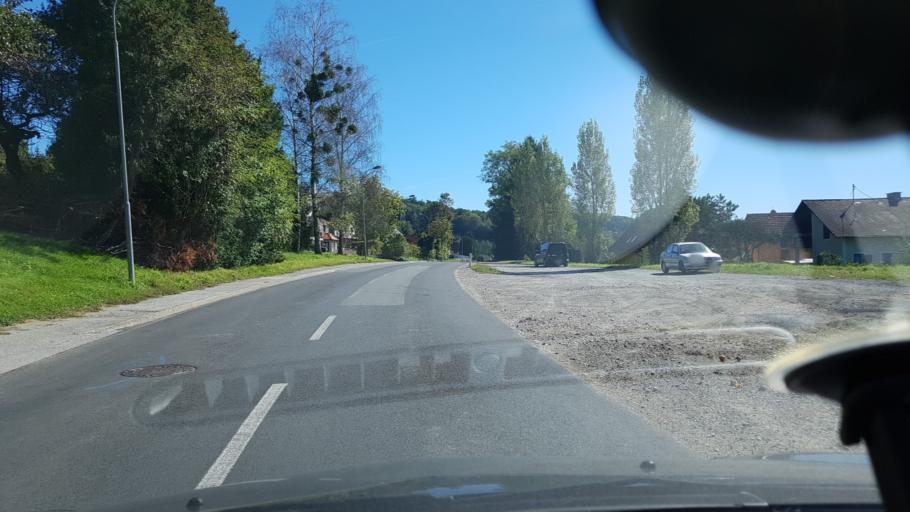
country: AT
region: Styria
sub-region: Politischer Bezirk Weiz
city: Sinabelkirchen
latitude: 47.1205
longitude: 15.8148
